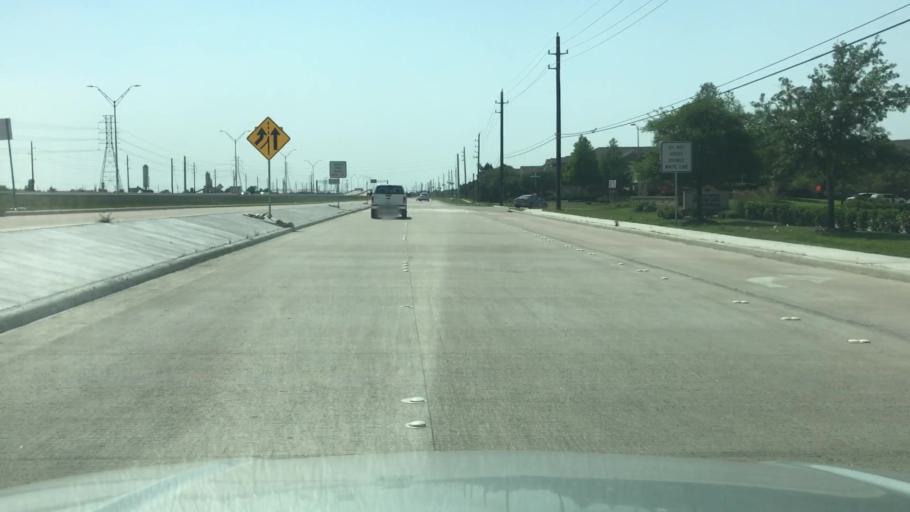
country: US
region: Texas
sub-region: Fort Bend County
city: Cinco Ranch
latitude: 29.6985
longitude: -95.8042
